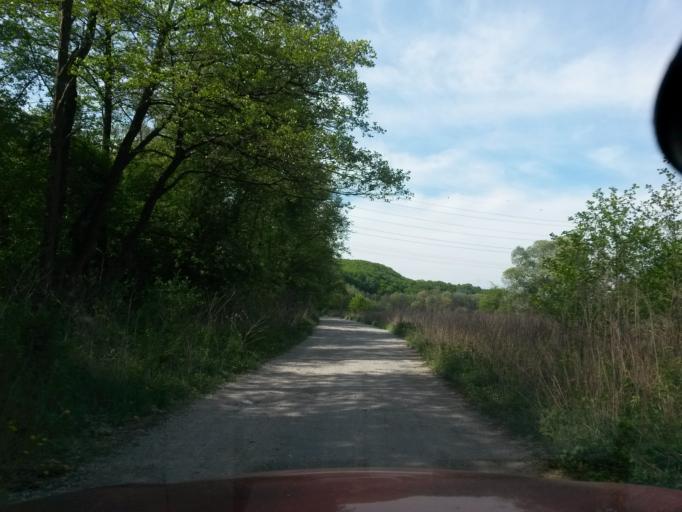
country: SK
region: Kosicky
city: Kosice
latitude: 48.7751
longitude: 21.2423
